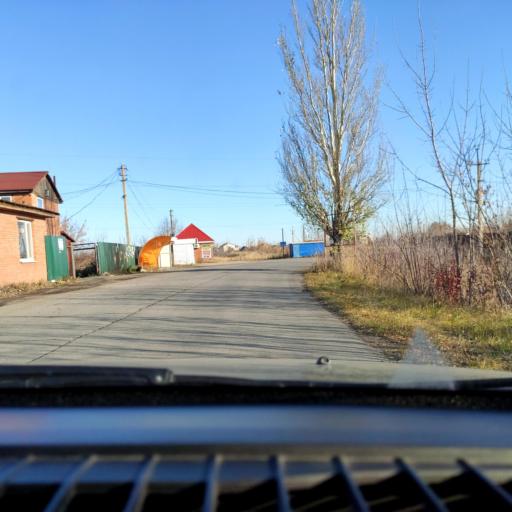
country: RU
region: Samara
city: Tol'yatti
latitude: 53.6640
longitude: 49.3366
